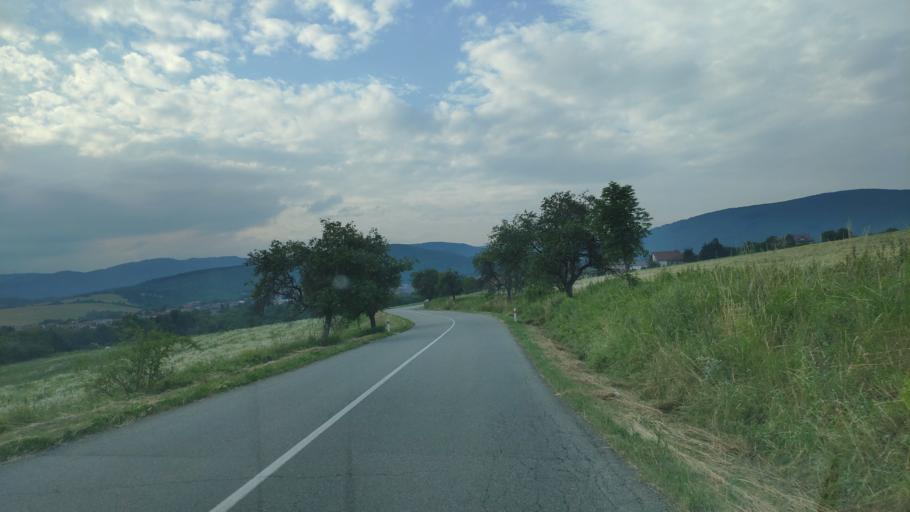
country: SK
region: Kosicky
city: Medzev
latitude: 48.7006
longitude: 20.9743
